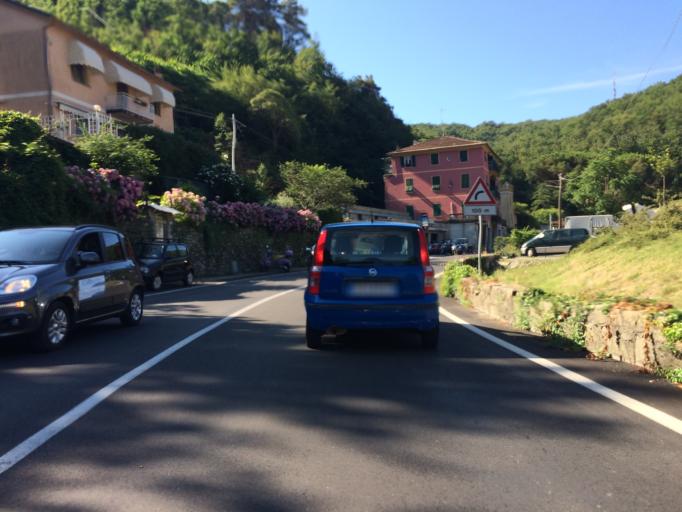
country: IT
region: Liguria
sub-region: Provincia di Genova
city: Camogli
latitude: 44.3423
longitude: 9.1753
